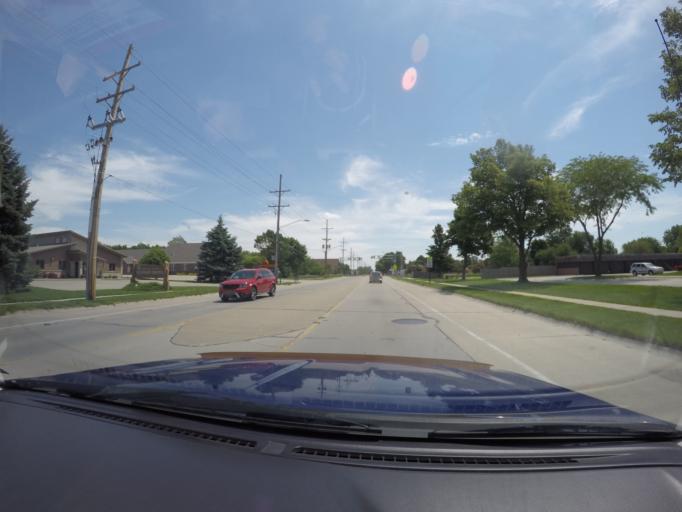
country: US
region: Nebraska
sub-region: Hall County
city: Grand Island
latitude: 40.9024
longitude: -98.3697
